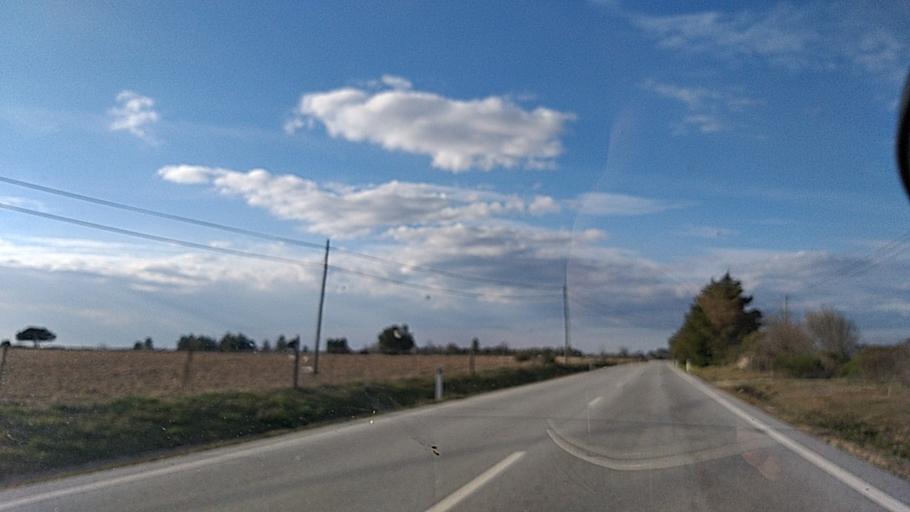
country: ES
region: Castille and Leon
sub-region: Provincia de Salamanca
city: Fuentes de Onoro
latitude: 40.6286
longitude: -6.8511
